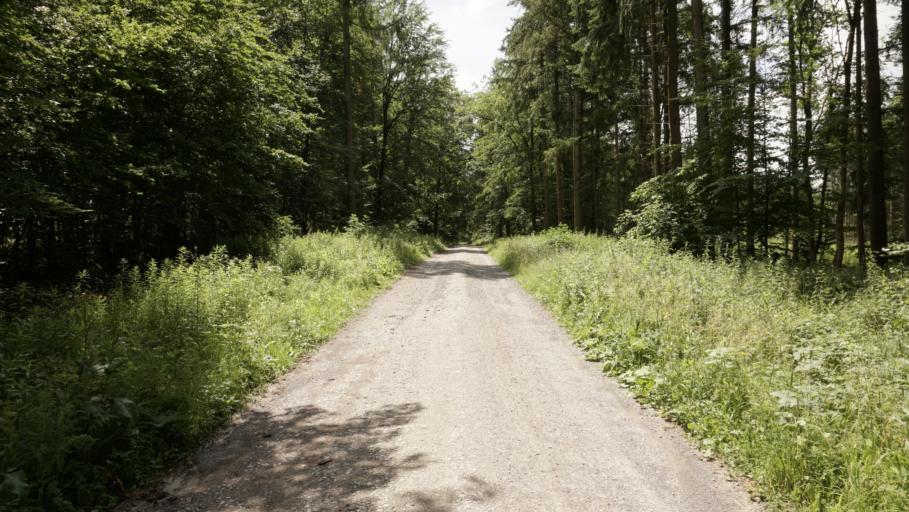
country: DE
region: Baden-Wuerttemberg
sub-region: Karlsruhe Region
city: Mosbach
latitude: 49.3334
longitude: 9.1931
